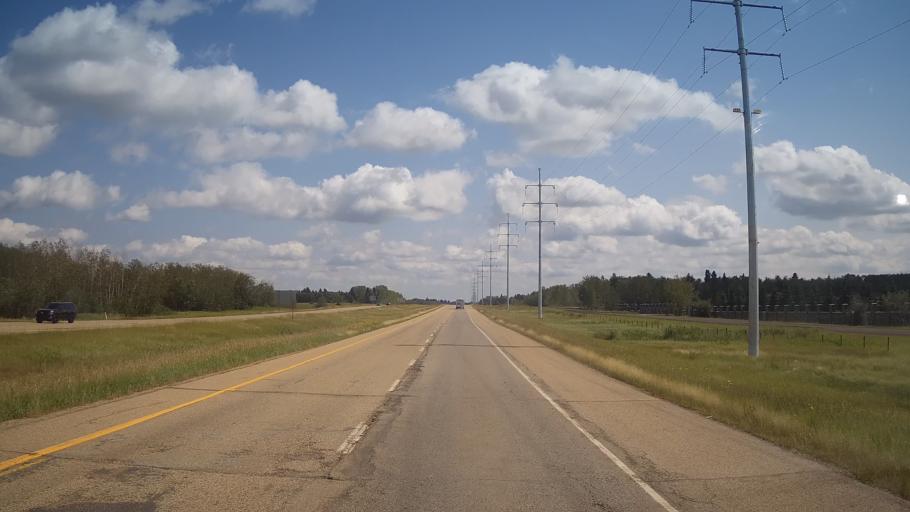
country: CA
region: Alberta
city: Sherwood Park
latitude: 53.4450
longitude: -113.2343
